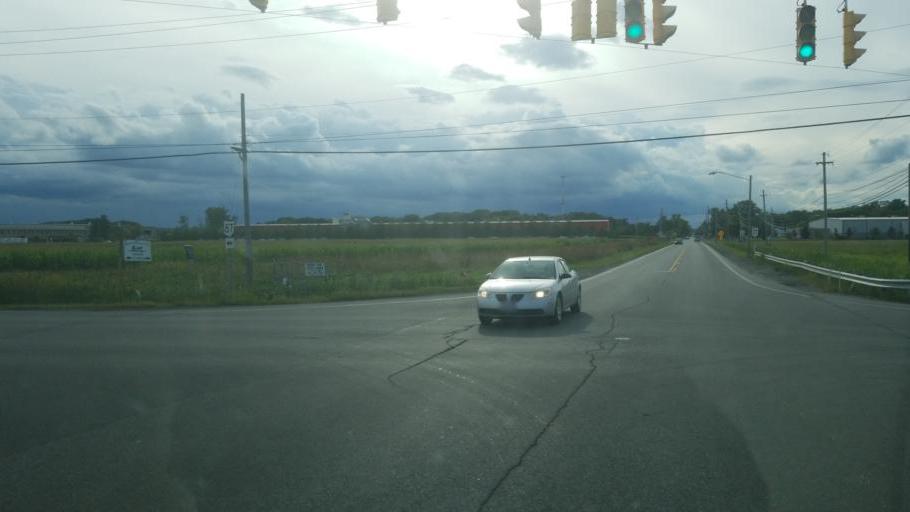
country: US
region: Ohio
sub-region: Geauga County
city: Middlefield
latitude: 41.4606
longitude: -81.0512
